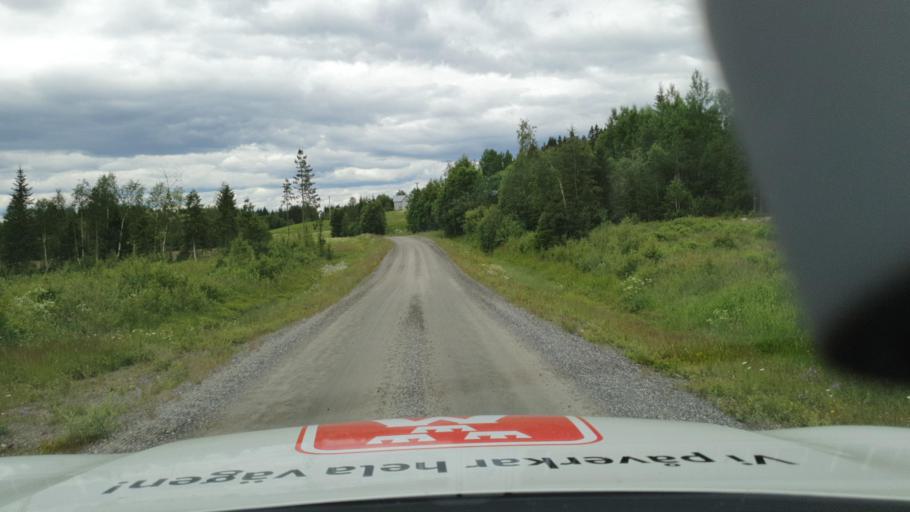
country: SE
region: Vaesterbotten
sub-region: Bjurholms Kommun
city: Bjurholm
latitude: 63.7317
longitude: 19.3028
